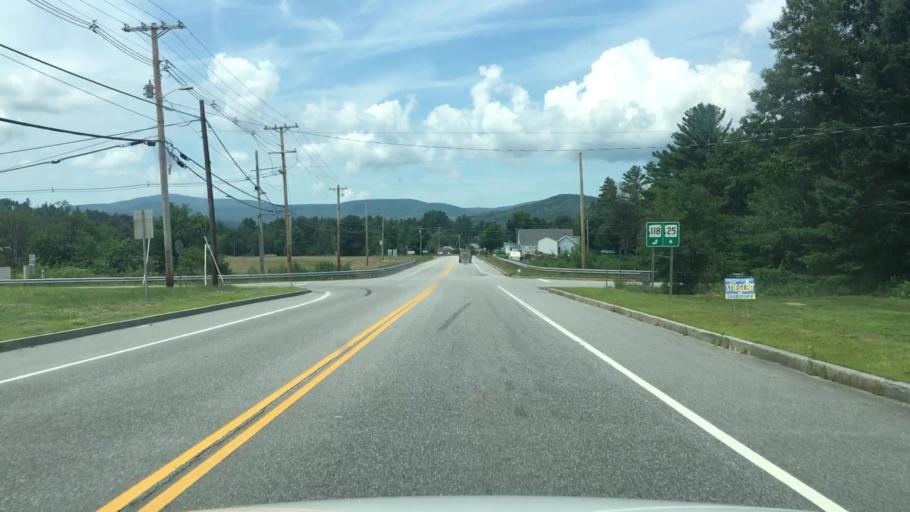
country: US
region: New Hampshire
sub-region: Grafton County
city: Rumney
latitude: 43.8195
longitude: -71.8839
